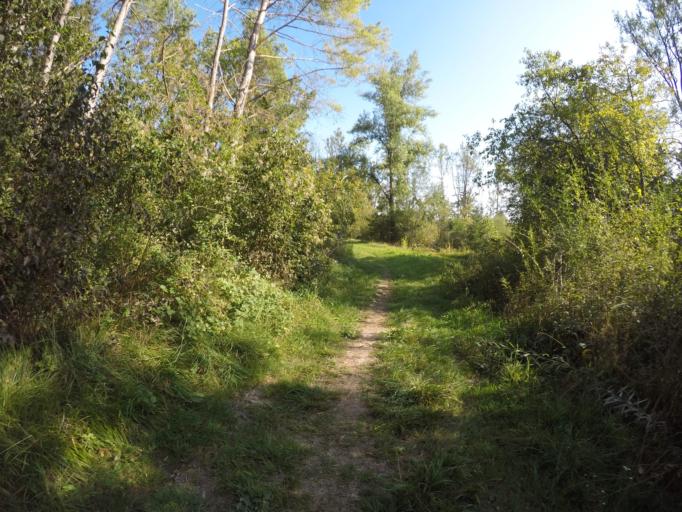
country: DE
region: Bavaria
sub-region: Lower Bavaria
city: Bruckberg
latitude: 48.4949
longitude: 11.9975
